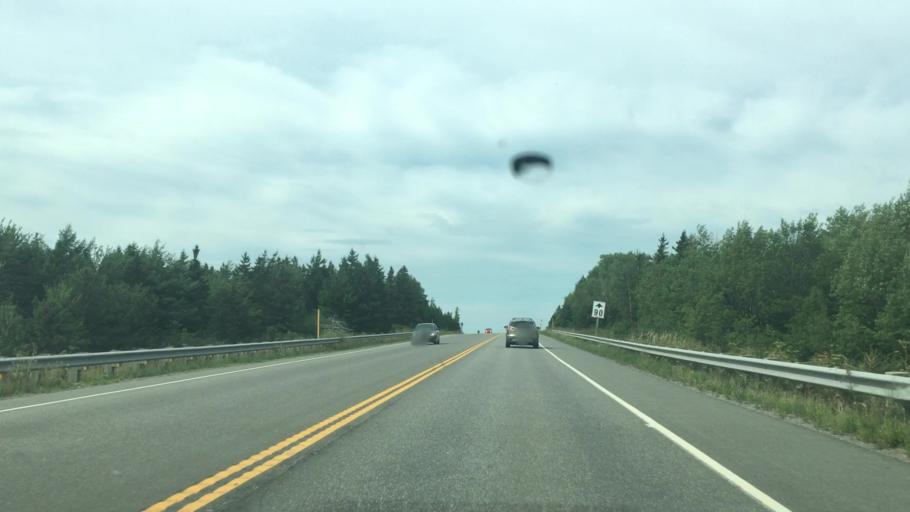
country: CA
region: Nova Scotia
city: Antigonish
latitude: 45.5895
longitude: -61.7796
